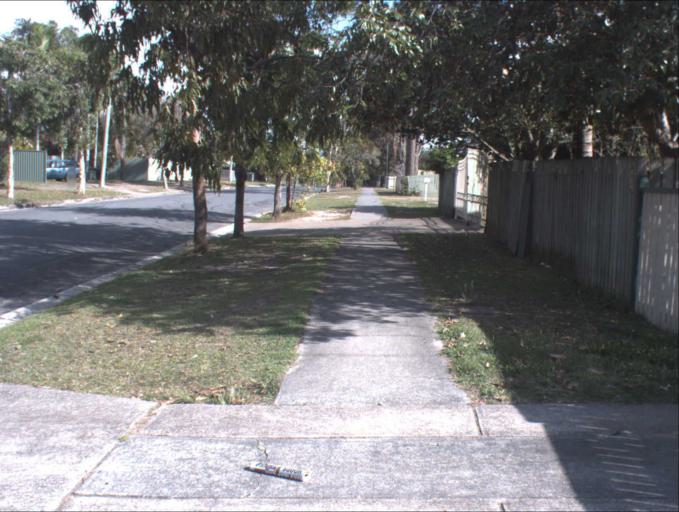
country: AU
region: Queensland
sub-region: Logan
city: Waterford West
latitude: -27.6714
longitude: 153.1327
